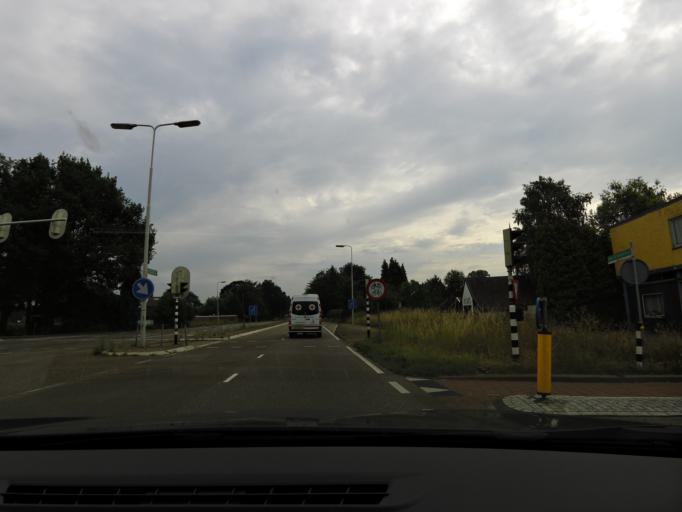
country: NL
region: Gelderland
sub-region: Gemeente Rheden
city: Dieren
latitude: 52.0457
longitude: 6.1050
